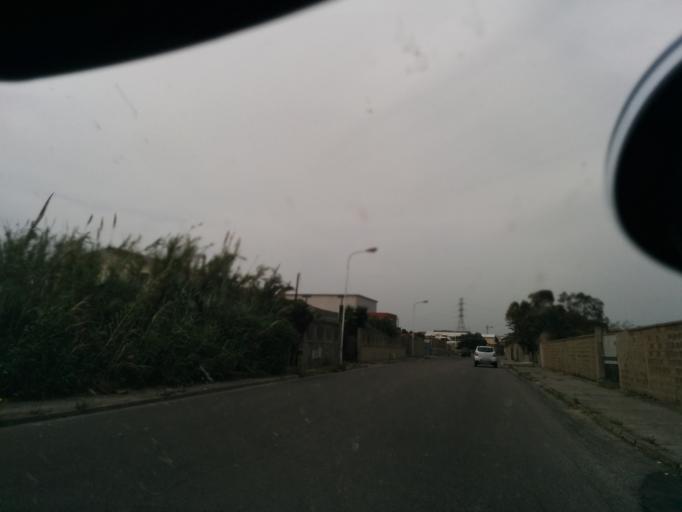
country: IT
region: Sardinia
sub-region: Provincia di Carbonia-Iglesias
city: Sant'Antioco
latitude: 39.0522
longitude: 8.4583
